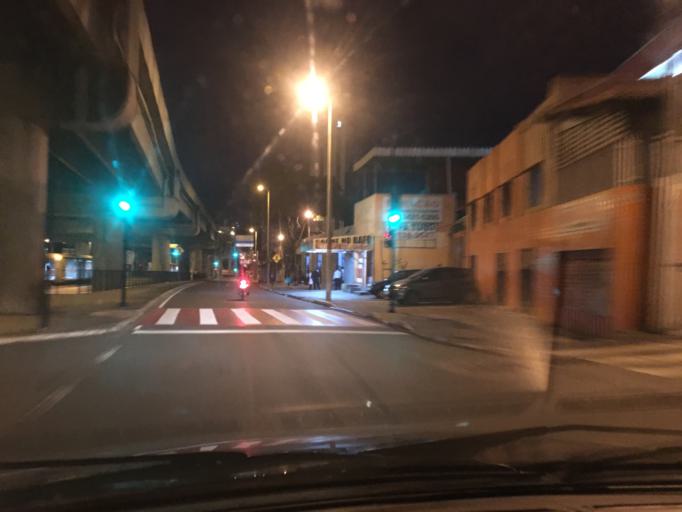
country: BR
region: Minas Gerais
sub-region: Belo Horizonte
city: Belo Horizonte
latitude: -19.9044
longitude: -43.9338
